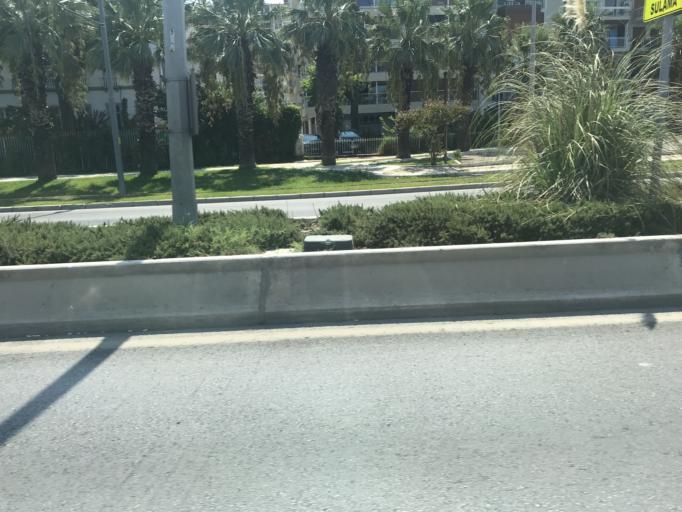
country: TR
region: Izmir
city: Izmir
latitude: 38.4018
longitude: 27.0927
